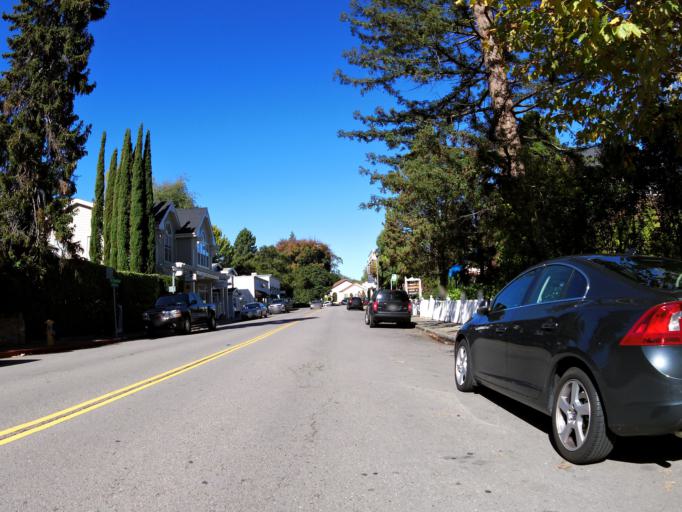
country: US
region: California
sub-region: Marin County
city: Ross
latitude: 37.9598
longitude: -122.5551
